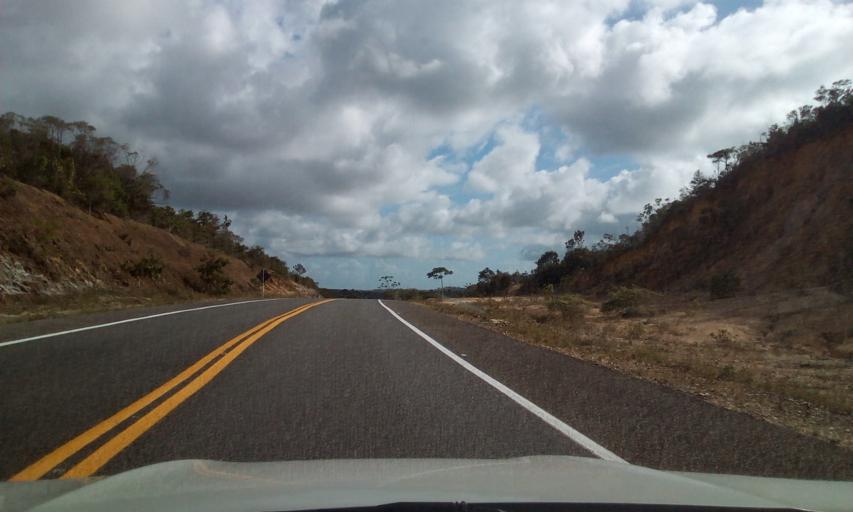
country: BR
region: Sergipe
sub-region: Indiaroba
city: Indiaroba
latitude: -11.6656
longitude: -37.5579
